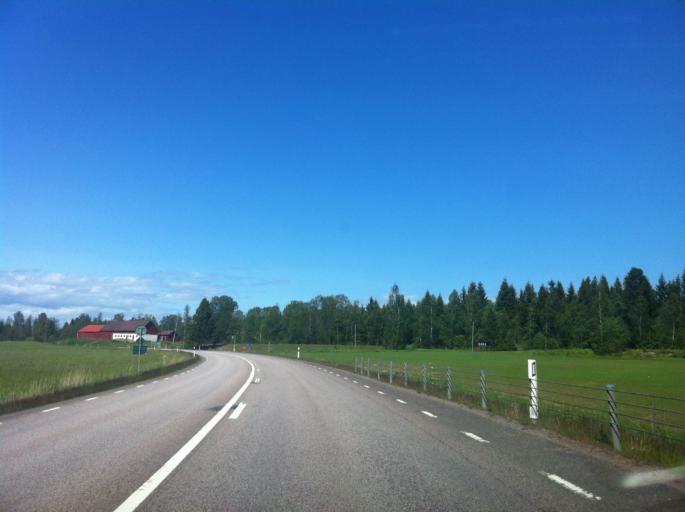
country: SE
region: Vaestra Goetaland
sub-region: Gullspangs Kommun
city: Gullspang
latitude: 58.9909
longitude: 14.1002
